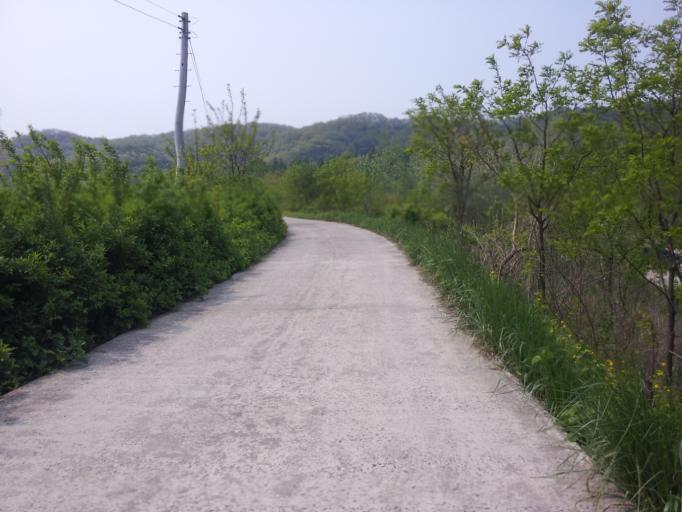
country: KR
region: Daejeon
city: Daejeon
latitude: 36.2792
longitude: 127.3347
